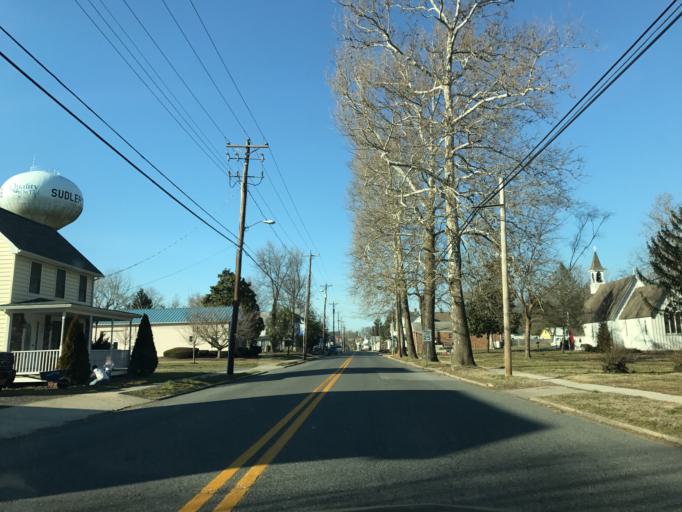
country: US
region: Maryland
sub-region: Queen Anne's County
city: Kingstown
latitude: 39.1842
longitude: -75.8584
